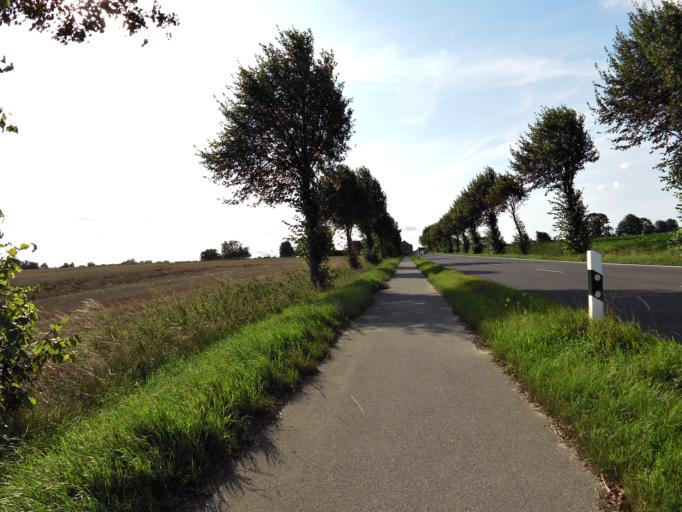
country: DE
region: North Rhine-Westphalia
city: Siersdorf
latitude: 50.8896
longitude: 6.2340
